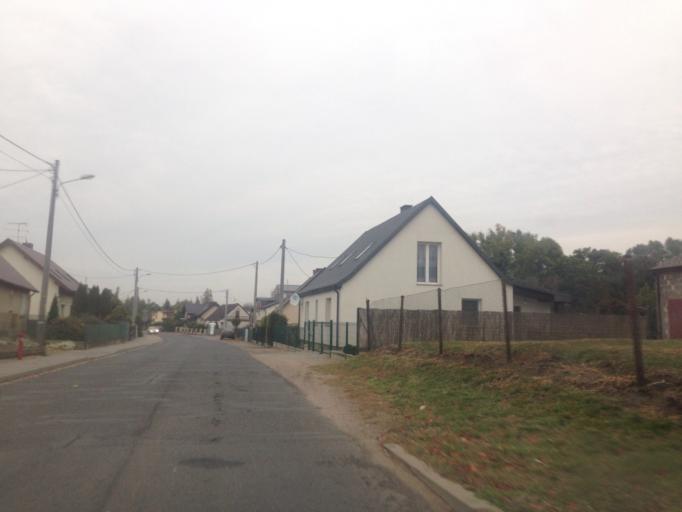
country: PL
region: Greater Poland Voivodeship
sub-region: Powiat gnieznienski
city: Lubowo
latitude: 52.4899
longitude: 17.4278
